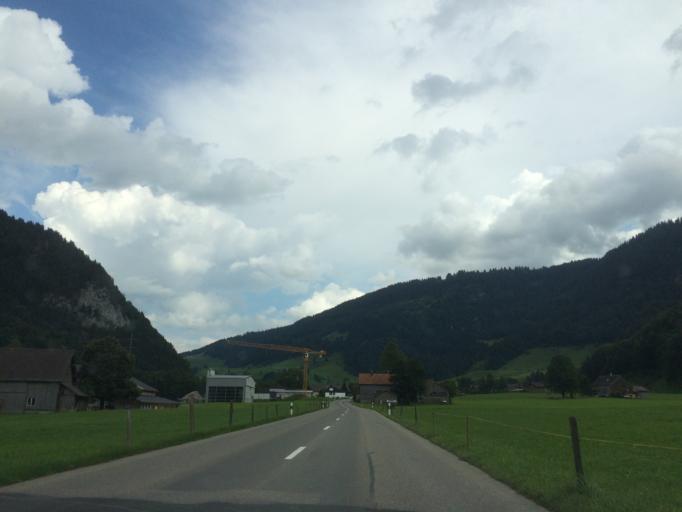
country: CH
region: Saint Gallen
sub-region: Wahlkreis Sarganserland
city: Quarten
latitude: 47.1872
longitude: 9.2435
